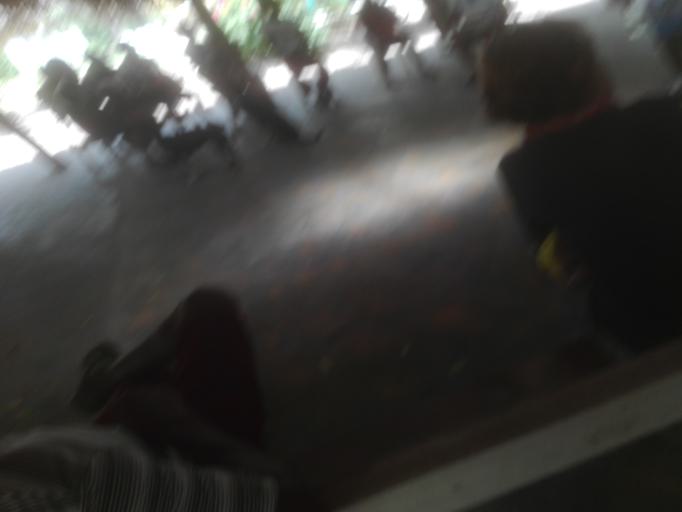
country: CO
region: Bolivar
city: Turbana
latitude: 10.1776
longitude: -75.7301
